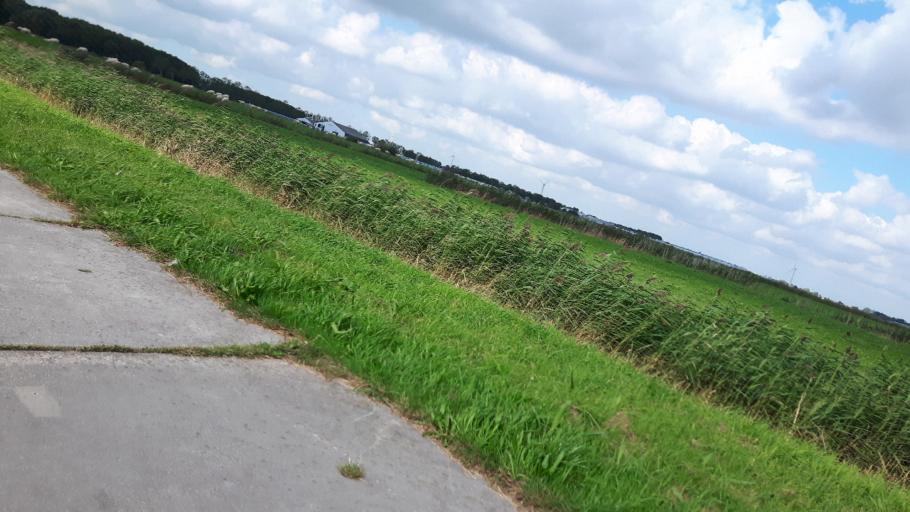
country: NL
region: North Holland
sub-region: Gemeente Enkhuizen
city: Enkhuizen
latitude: 52.7153
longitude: 5.2133
